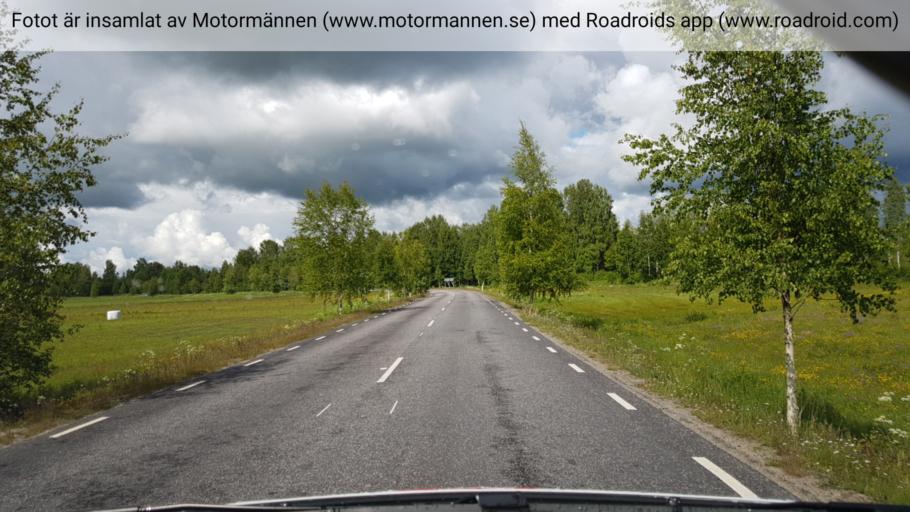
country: SE
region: Vaesterbotten
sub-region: Vannas Kommun
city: Vannasby
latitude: 63.8884
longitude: 19.8891
